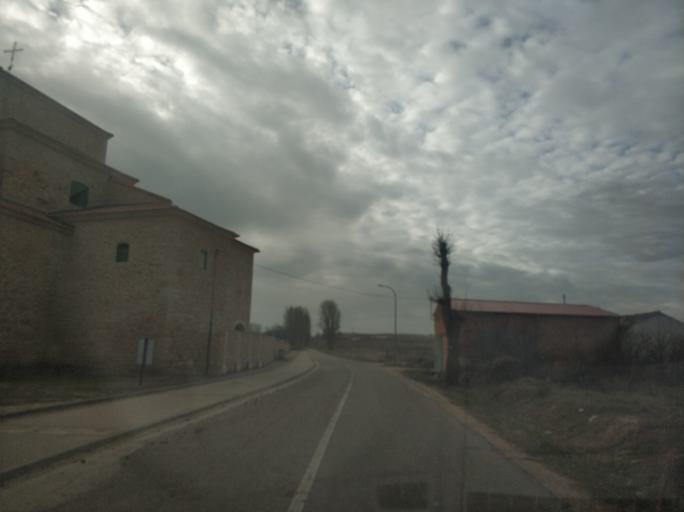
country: ES
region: Castille and Leon
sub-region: Provincia de Burgos
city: Penaranda de Duero
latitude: 41.6829
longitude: -3.4798
